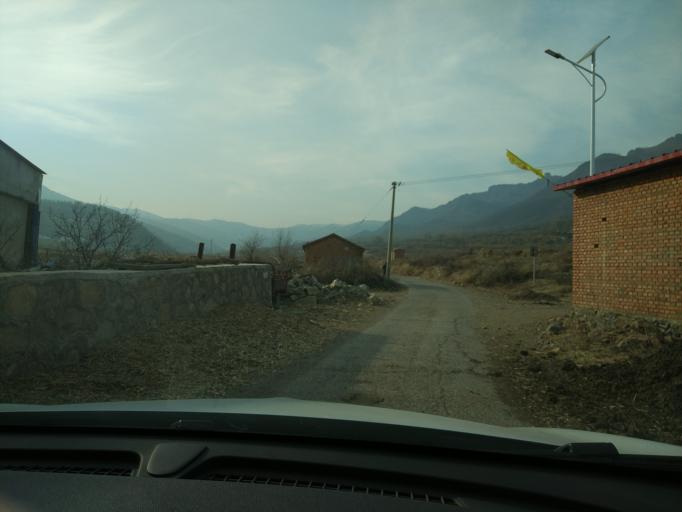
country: CN
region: Hebei
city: Xiwanzi
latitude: 40.8232
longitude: 115.4964
